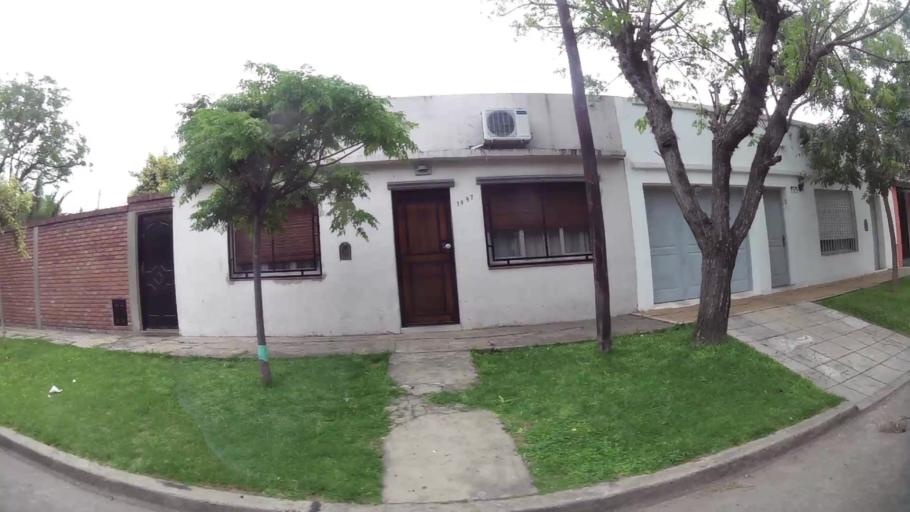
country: AR
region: Buenos Aires
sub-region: Partido de Campana
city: Campana
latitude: -34.1776
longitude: -58.9560
